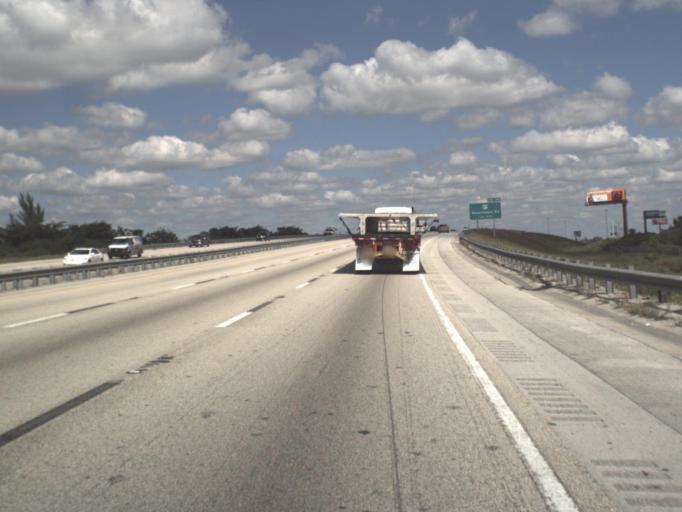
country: US
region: Florida
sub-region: Miami-Dade County
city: Hialeah Gardens
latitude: 25.8897
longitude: -80.3886
